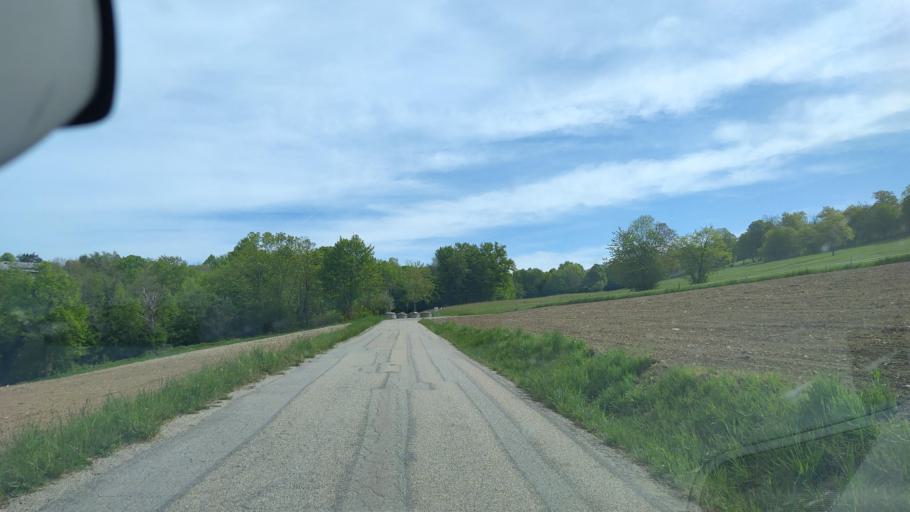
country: FR
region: Rhone-Alpes
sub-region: Departement de la Savoie
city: Mouxy
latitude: 45.6999
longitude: 5.9522
